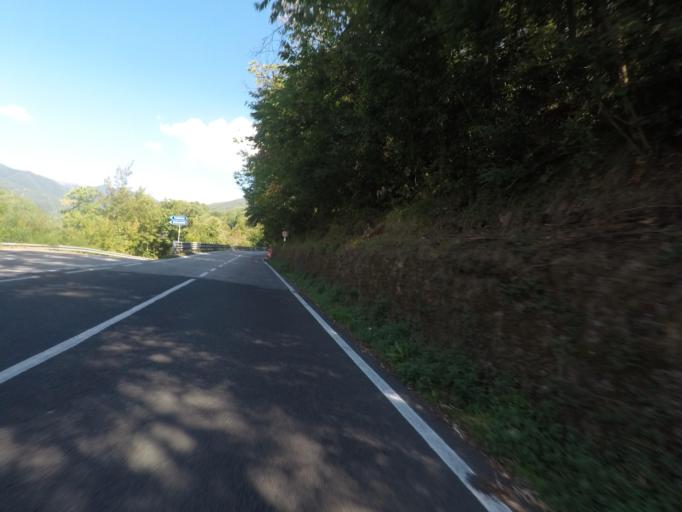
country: IT
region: Tuscany
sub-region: Provincia di Massa-Carrara
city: Fivizzano
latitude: 44.2425
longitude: 10.1406
